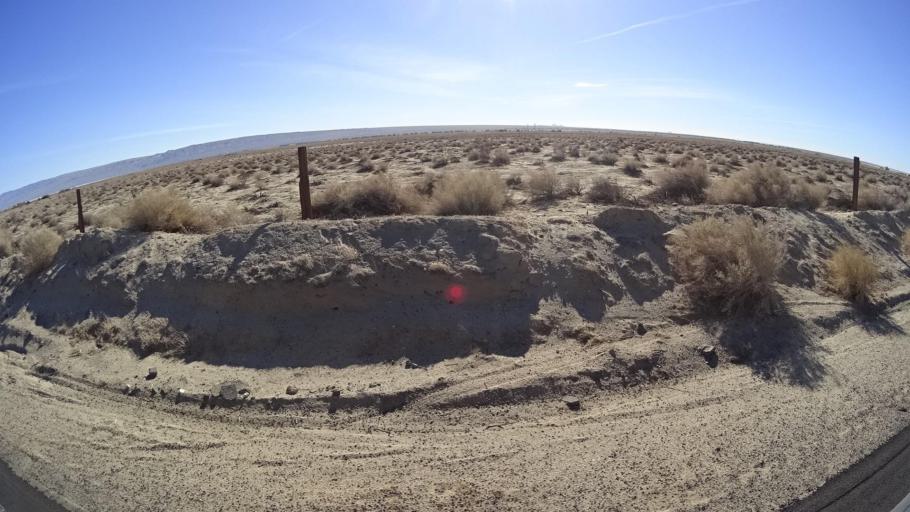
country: US
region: California
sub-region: Kern County
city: California City
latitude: 35.3026
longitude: -117.9783
